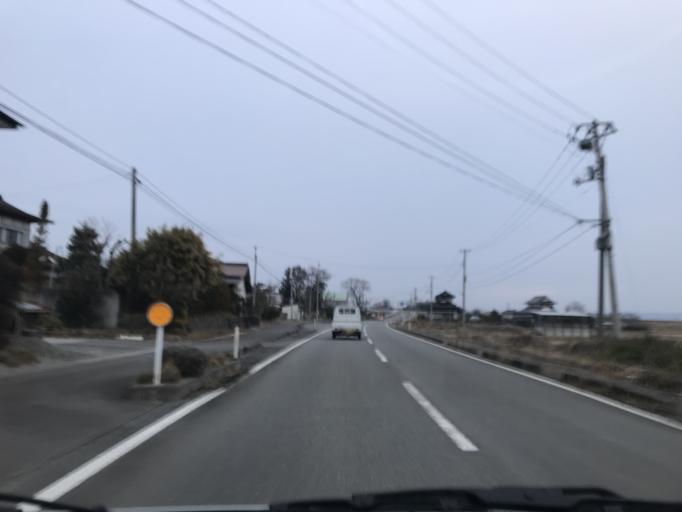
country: JP
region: Miyagi
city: Wakuya
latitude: 38.7221
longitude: 141.1464
